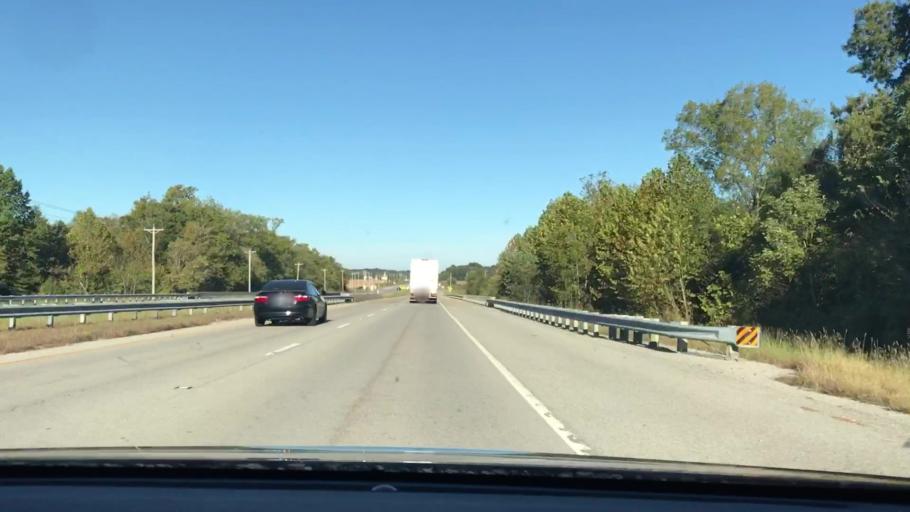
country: US
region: Kentucky
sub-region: Christian County
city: Hopkinsville
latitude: 36.8321
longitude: -87.5239
